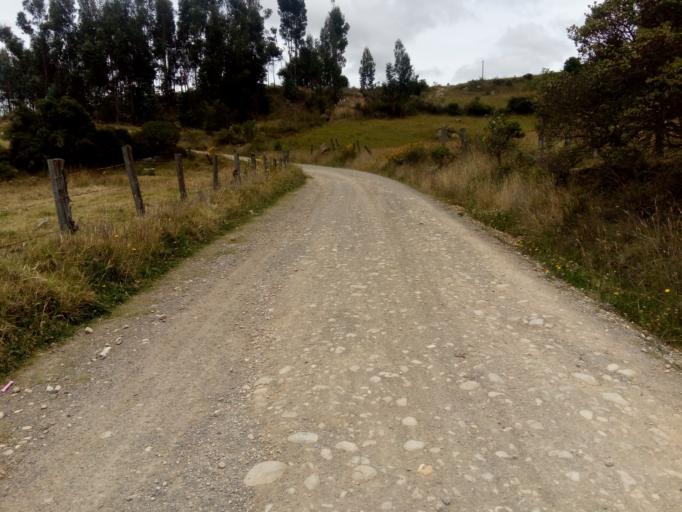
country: CO
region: Boyaca
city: Gameza
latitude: 5.8225
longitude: -72.8006
